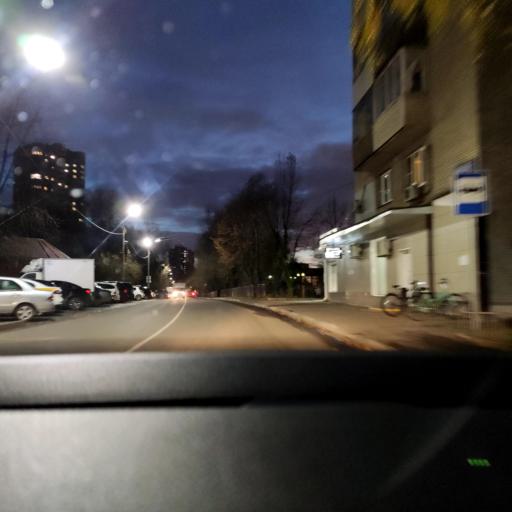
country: RU
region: Moskovskaya
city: Reutov
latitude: 55.7673
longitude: 37.8573
